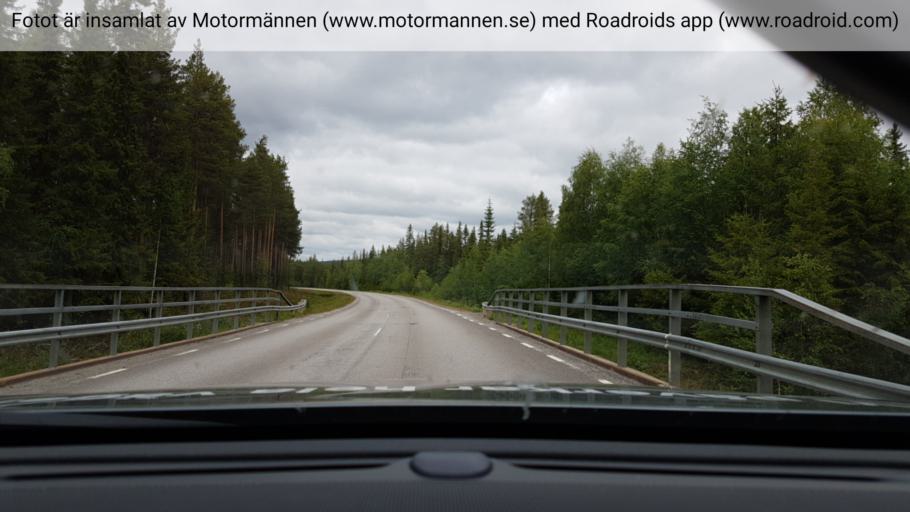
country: SE
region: Vaesterbotten
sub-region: Sorsele Kommun
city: Sorsele
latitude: 65.6150
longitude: 17.4938
